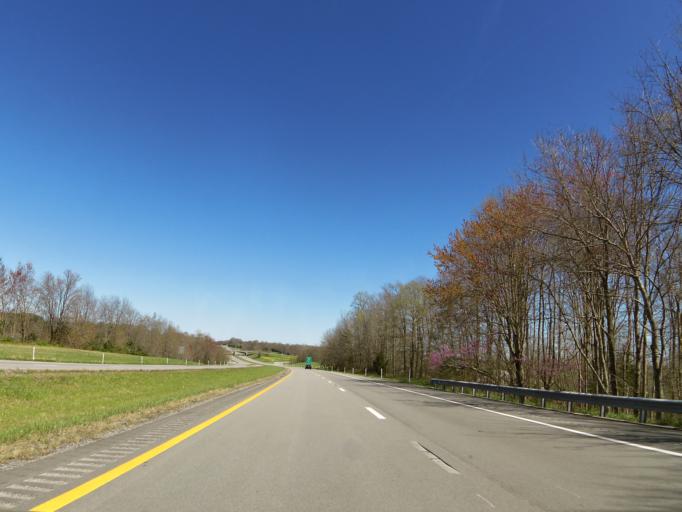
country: US
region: Kentucky
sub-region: Pulaski County
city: Somerset
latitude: 37.0915
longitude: -84.8097
